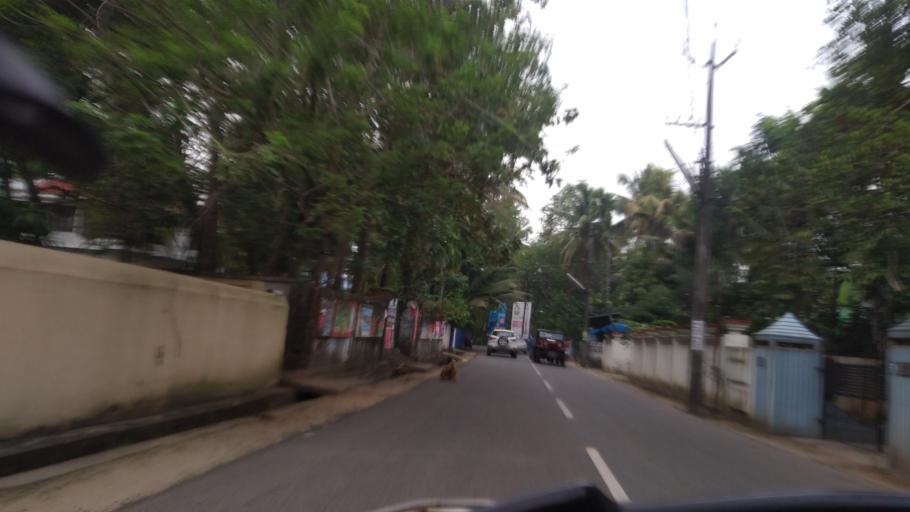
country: IN
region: Kerala
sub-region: Thrissur District
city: Kodungallur
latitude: 10.1394
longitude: 76.2188
